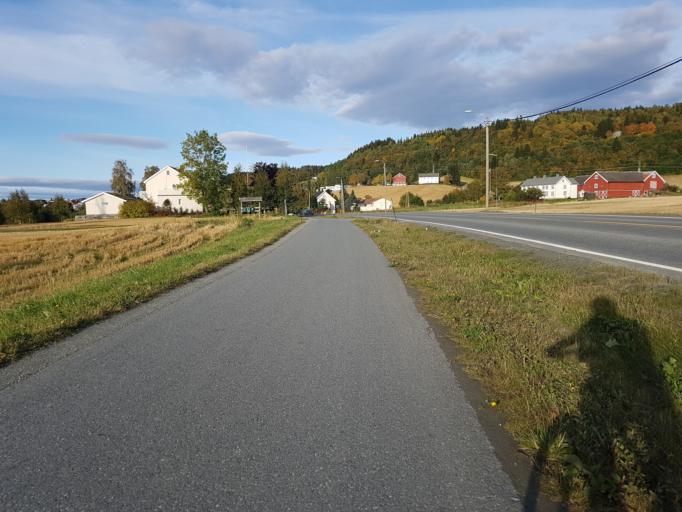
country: NO
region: Sor-Trondelag
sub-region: Trondheim
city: Trondheim
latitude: 63.3777
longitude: 10.4329
